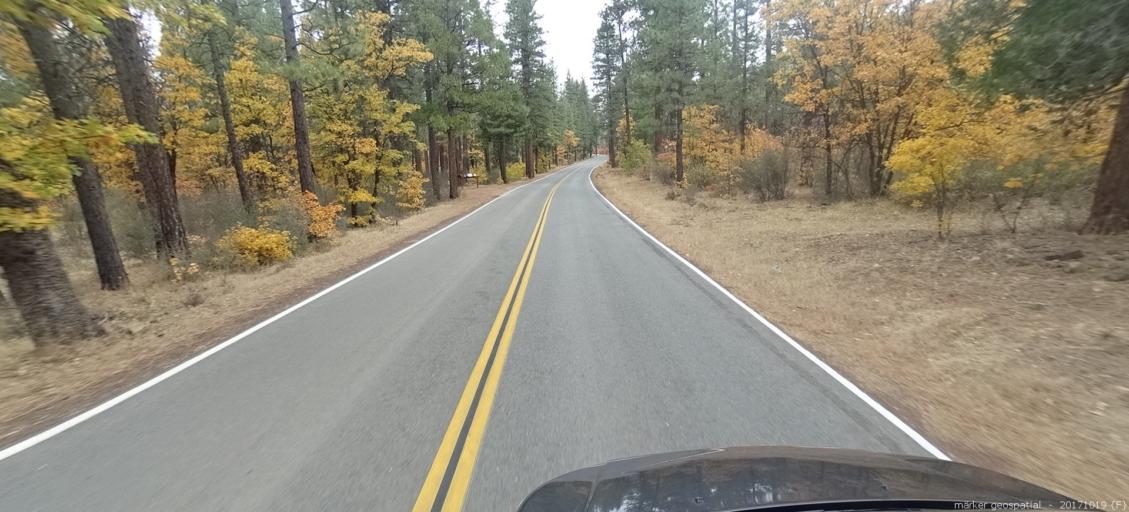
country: US
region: California
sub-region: Shasta County
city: Burney
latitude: 41.1808
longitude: -121.3629
